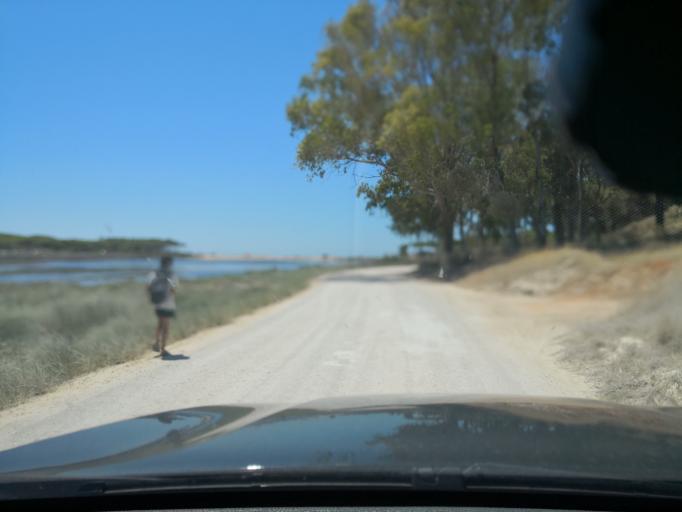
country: PT
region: Faro
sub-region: Loule
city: Quarteira
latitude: 37.0633
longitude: -8.0834
